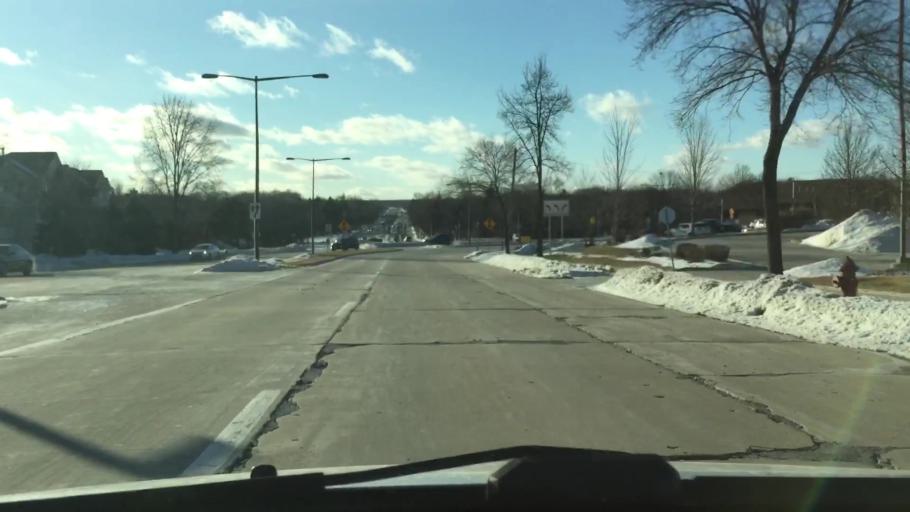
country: US
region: Wisconsin
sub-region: Milwaukee County
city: Greenfield
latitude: 42.9882
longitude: -88.0542
